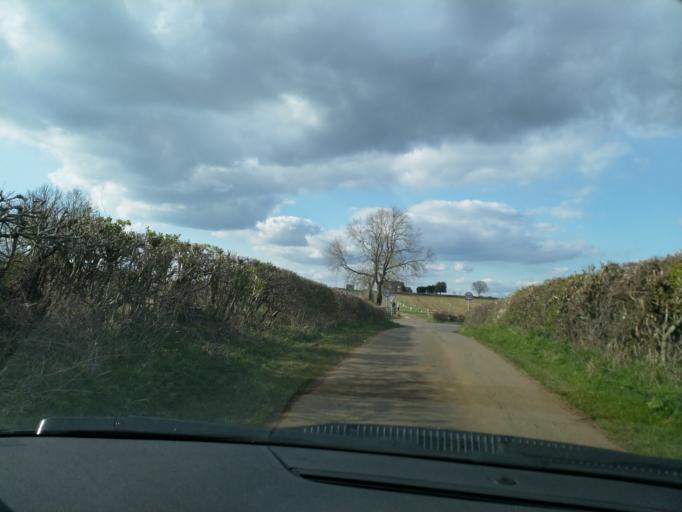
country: GB
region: England
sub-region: Oxfordshire
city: Banbury
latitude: 52.0836
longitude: -1.2640
